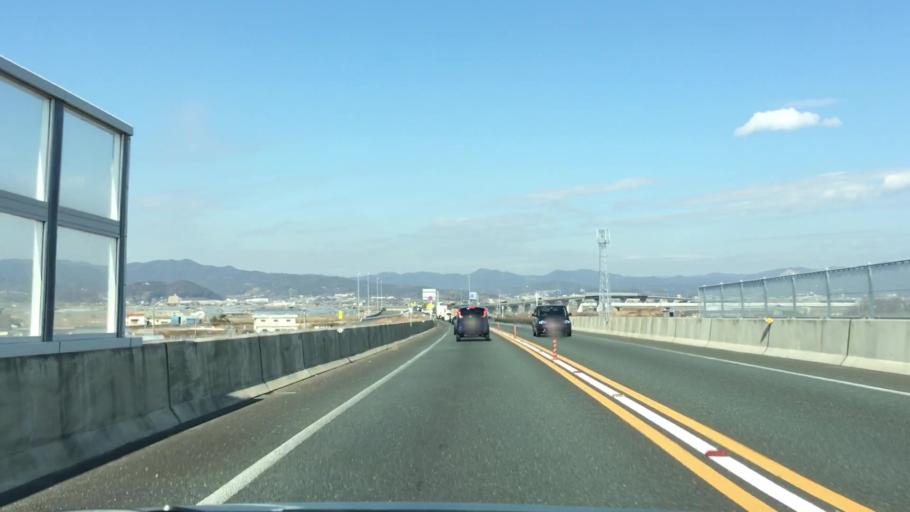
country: JP
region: Aichi
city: Kozakai-cho
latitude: 34.7873
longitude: 137.3324
